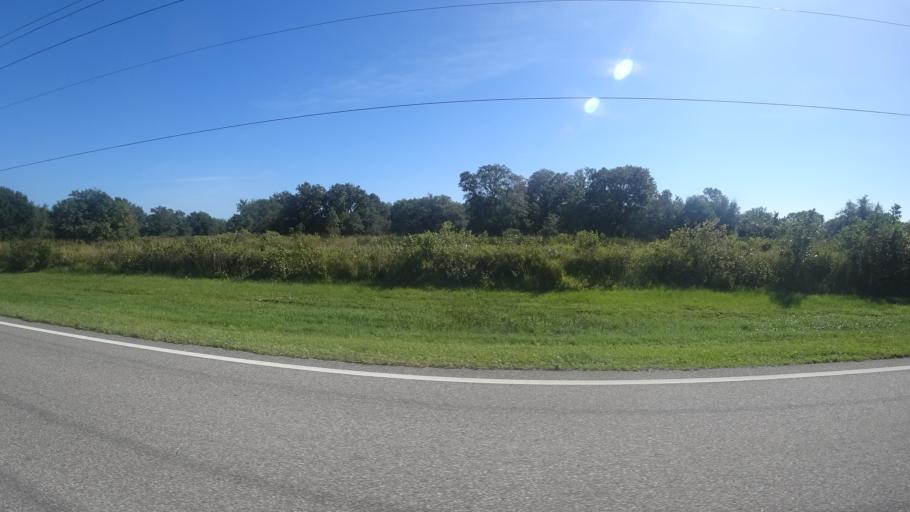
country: US
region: Florida
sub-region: Sarasota County
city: Lake Sarasota
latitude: 27.3708
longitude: -82.2684
